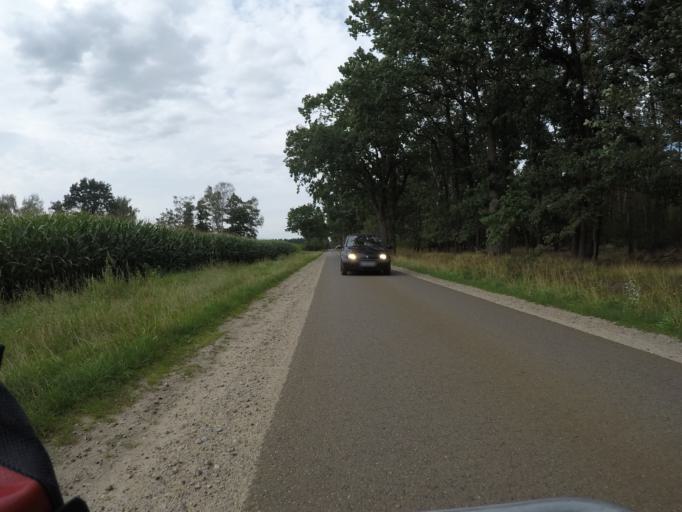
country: DE
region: Lower Saxony
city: Bardowick
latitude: 53.3094
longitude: 10.4024
